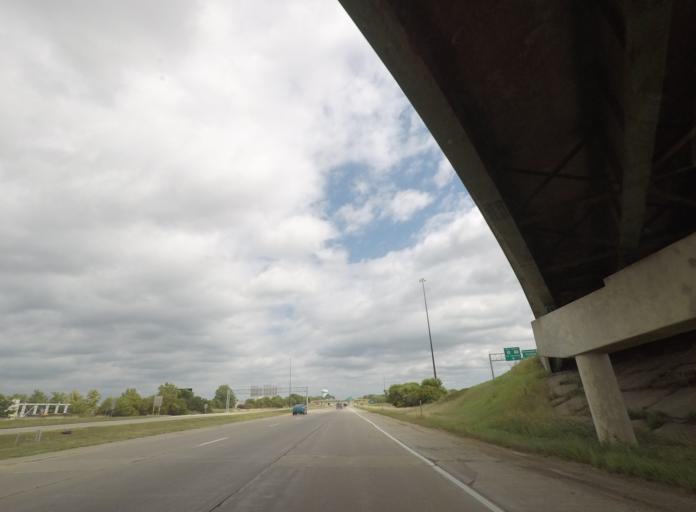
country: US
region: Iowa
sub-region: Linn County
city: Cedar Rapids
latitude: 41.9268
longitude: -91.6639
